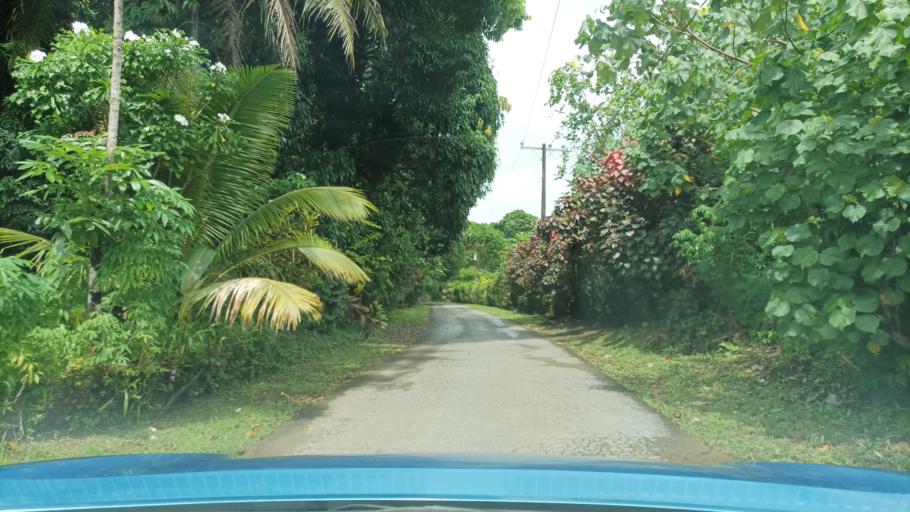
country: FM
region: Pohnpei
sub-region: Madolenihm Municipality
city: Madolenihm Municipality Government
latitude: 6.8846
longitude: 158.3203
